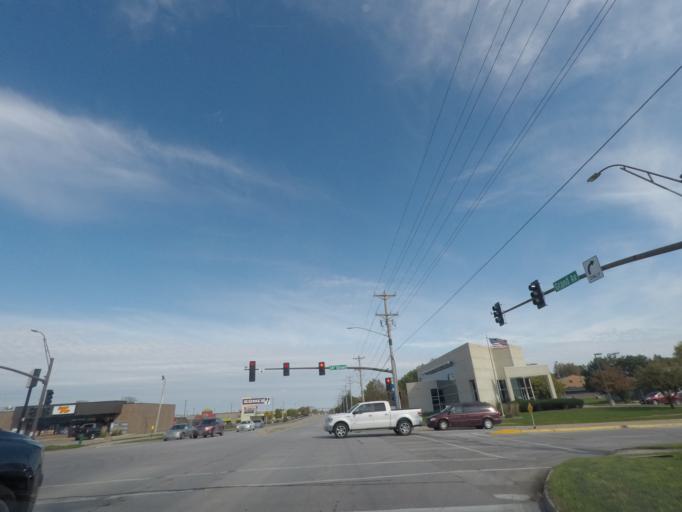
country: US
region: Iowa
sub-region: Story County
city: Ames
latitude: 42.0455
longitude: -93.6204
